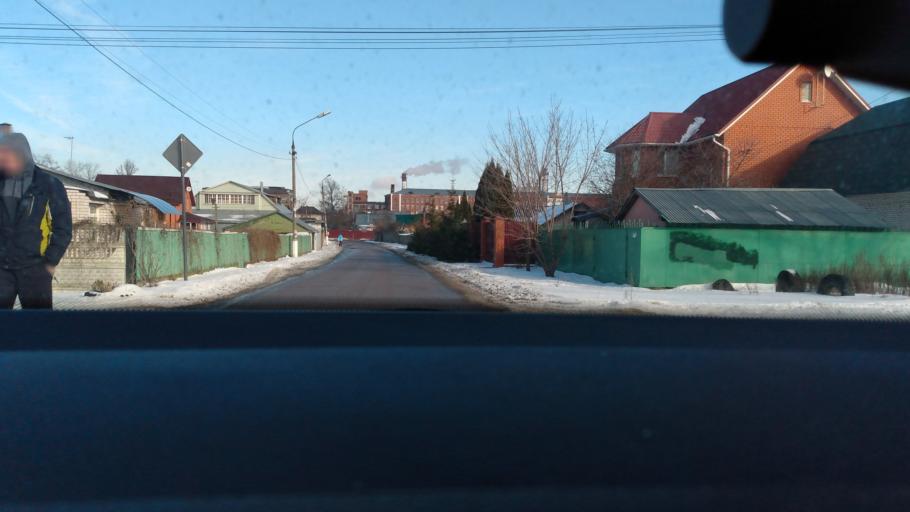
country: RU
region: Moskovskaya
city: Ramenskoye
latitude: 55.5668
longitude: 38.2125
